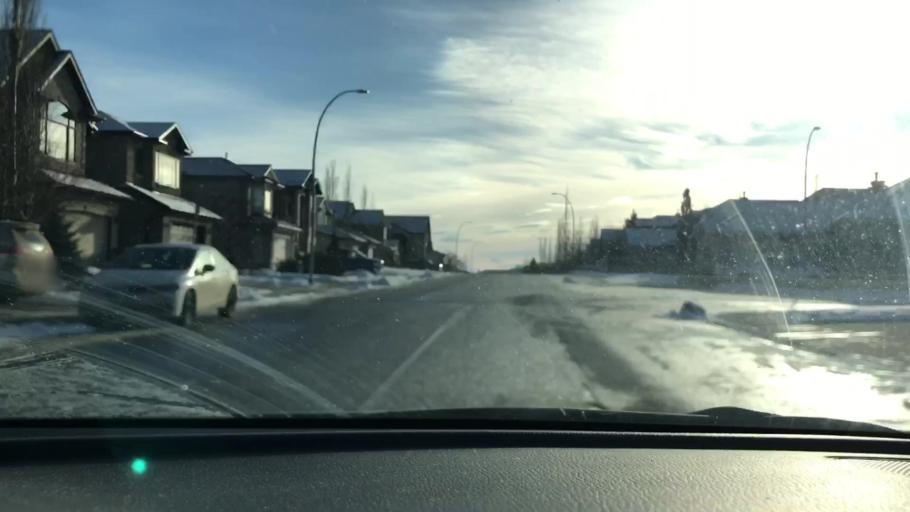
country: CA
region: Alberta
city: Calgary
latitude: 51.0255
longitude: -114.1772
